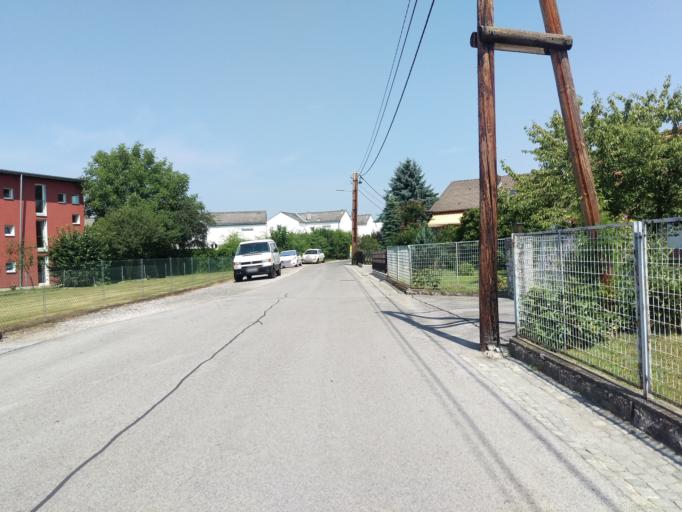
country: AT
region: Styria
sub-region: Politischer Bezirk Graz-Umgebung
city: Feldkirchen bei Graz
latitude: 47.0323
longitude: 15.4544
